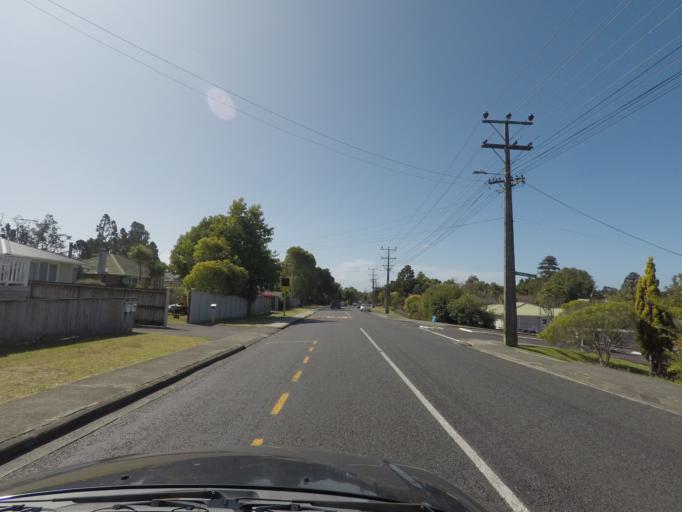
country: NZ
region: Auckland
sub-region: Auckland
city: Titirangi
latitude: -36.9289
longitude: 174.6548
